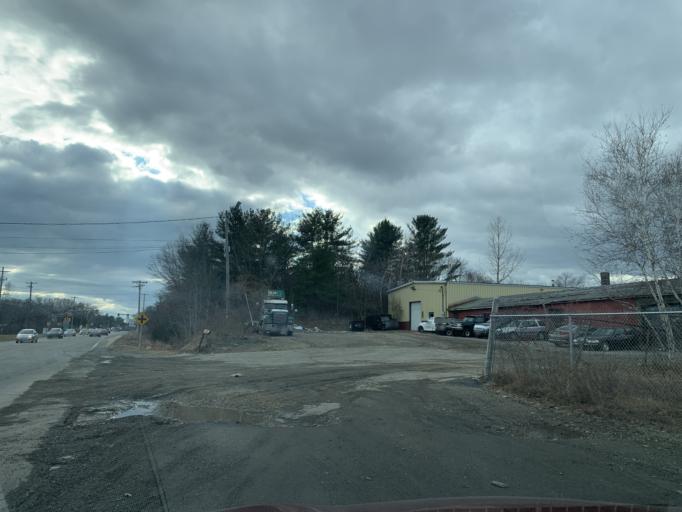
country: US
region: Massachusetts
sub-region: Essex County
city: Newburyport
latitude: 42.7914
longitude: -70.8781
